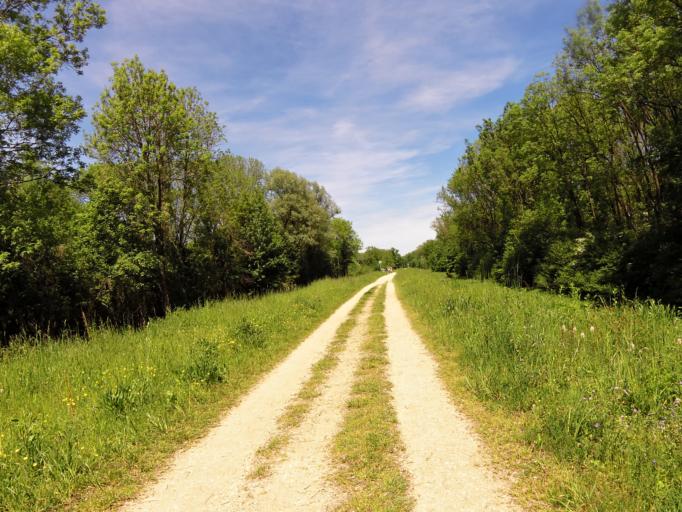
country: DE
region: Bavaria
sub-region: Upper Bavaria
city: Freising
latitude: 48.3862
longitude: 11.7410
